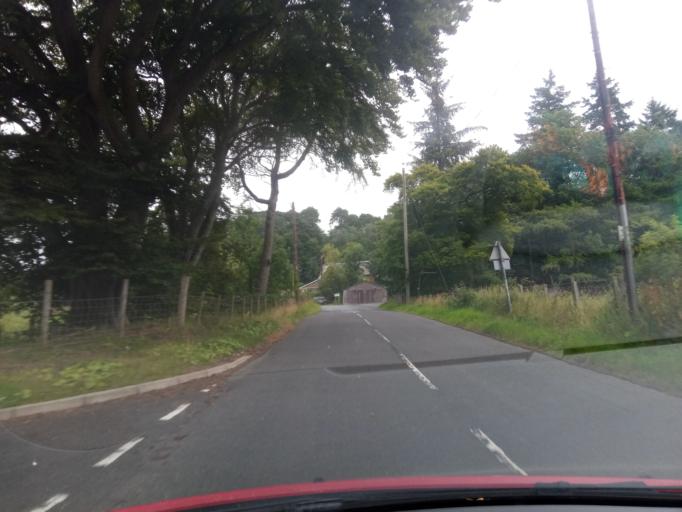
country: GB
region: Scotland
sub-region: The Scottish Borders
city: Galashiels
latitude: 55.6523
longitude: -2.8668
